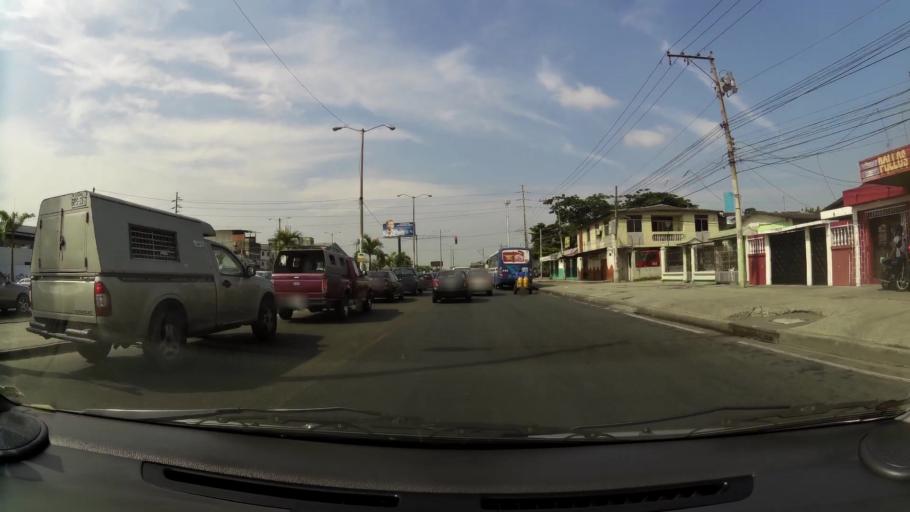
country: EC
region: Guayas
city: Guayaquil
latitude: -2.2456
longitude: -79.8956
